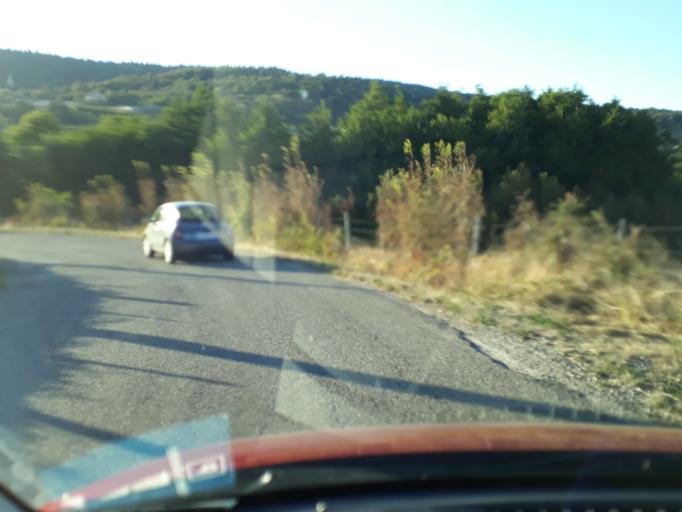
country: FR
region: Rhone-Alpes
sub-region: Departement de l'Ardeche
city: Felines
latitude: 45.3255
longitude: 4.7120
